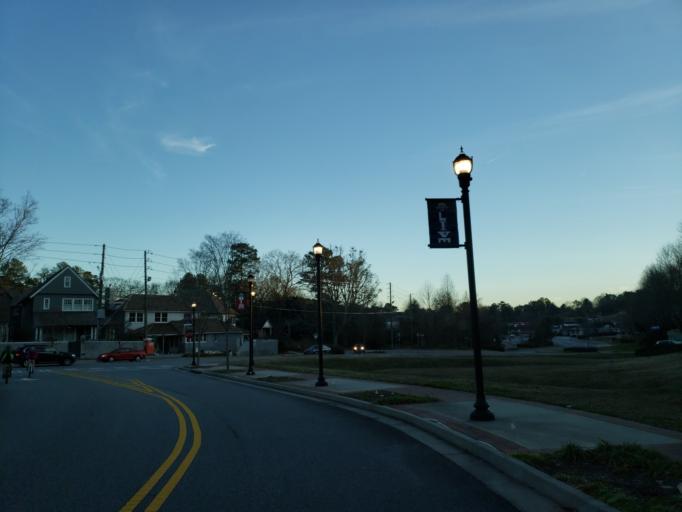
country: US
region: Georgia
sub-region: Fulton County
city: Alpharetta
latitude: 34.0731
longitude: -84.2930
